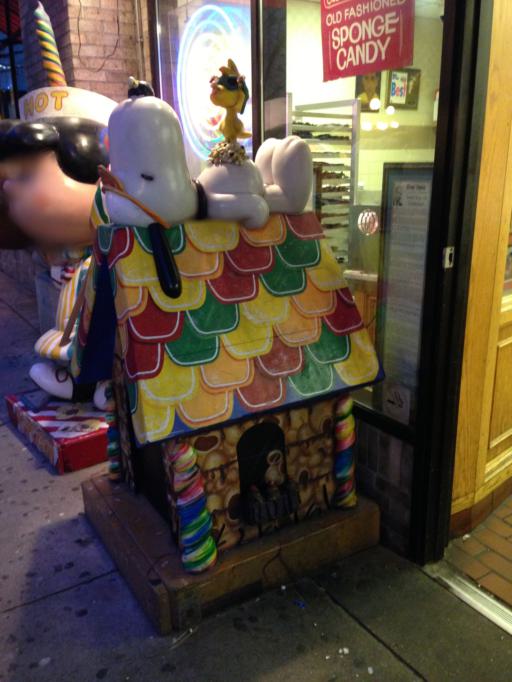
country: US
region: Minnesota
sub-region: Ramsey County
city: Saint Paul
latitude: 44.9478
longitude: -93.0962
